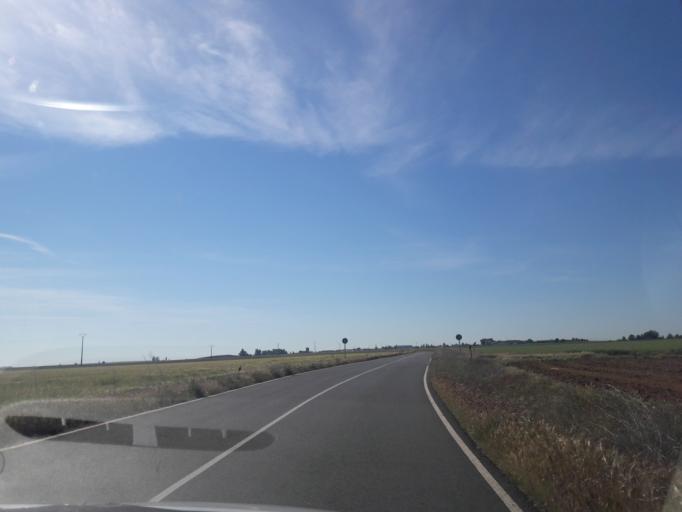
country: ES
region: Castille and Leon
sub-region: Provincia de Salamanca
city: Espino de la Orbada
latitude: 41.0919
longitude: -5.4129
